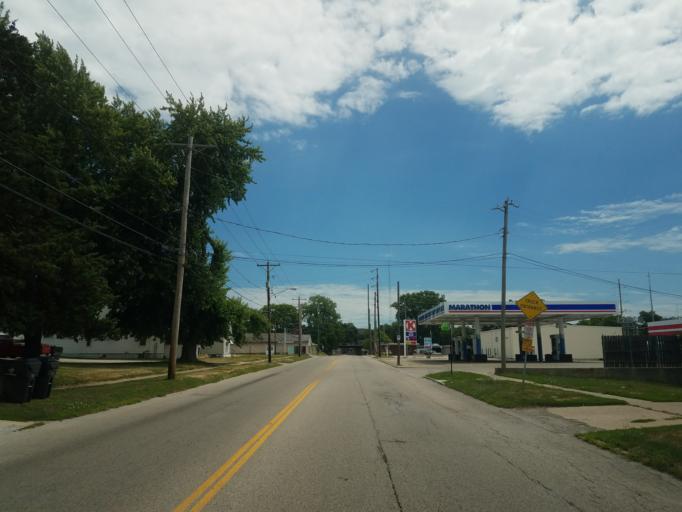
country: US
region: Illinois
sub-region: McLean County
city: Bloomington
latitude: 40.4825
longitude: -89.0095
